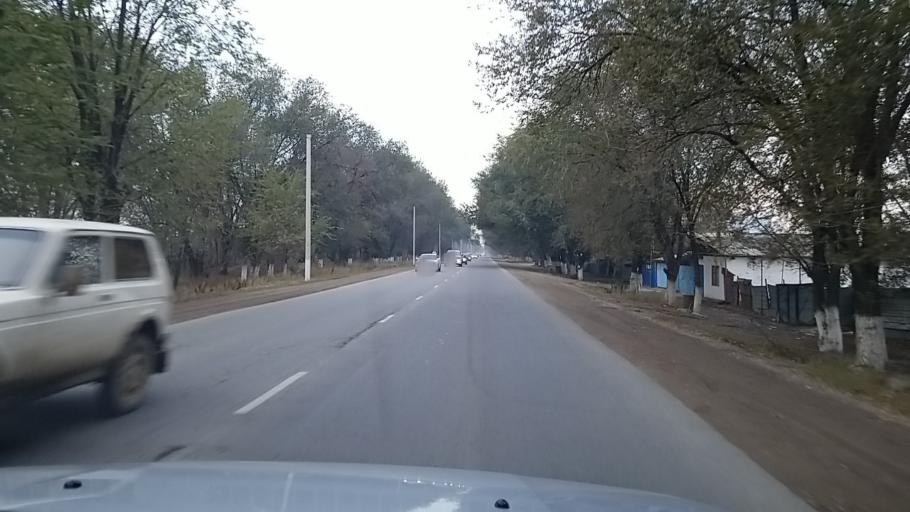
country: KZ
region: Almaty Oblysy
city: Burunday
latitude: 43.3548
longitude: 76.8107
